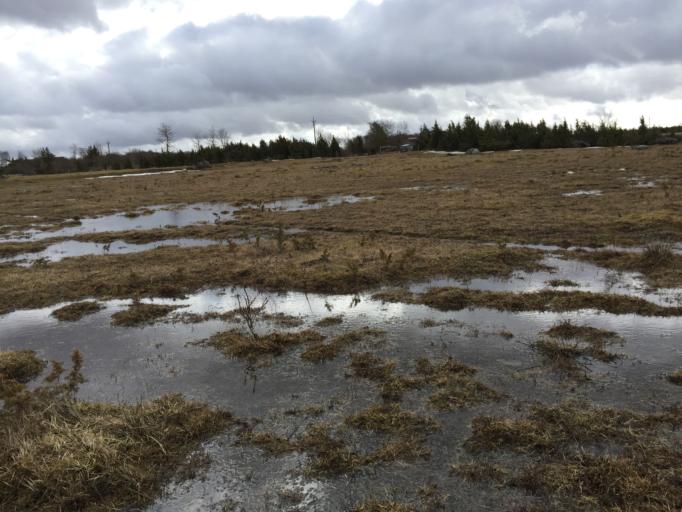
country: EE
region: Laeaene
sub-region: Ridala Parish
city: Uuemoisa
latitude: 58.7263
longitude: 23.5998
